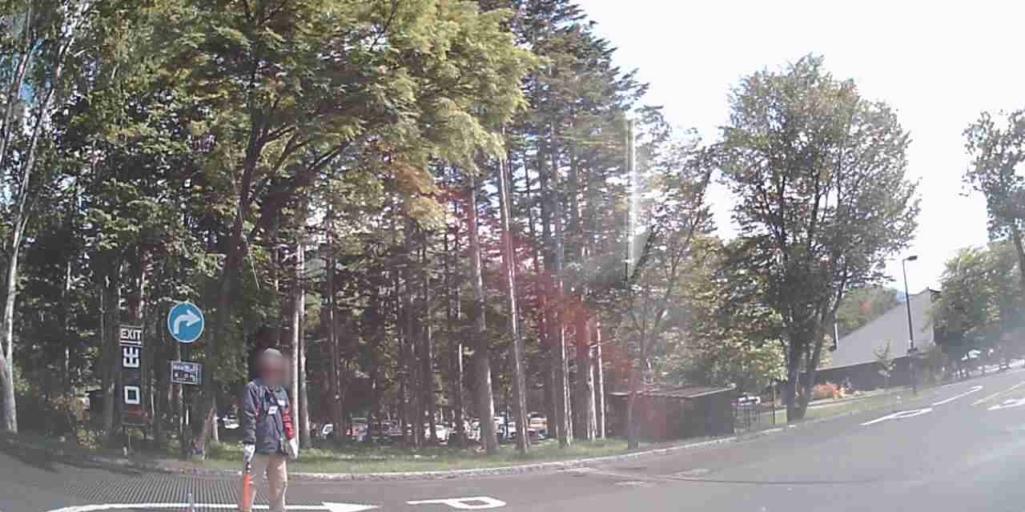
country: JP
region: Hokkaido
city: Shiraoi
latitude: 42.7734
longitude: 141.4048
